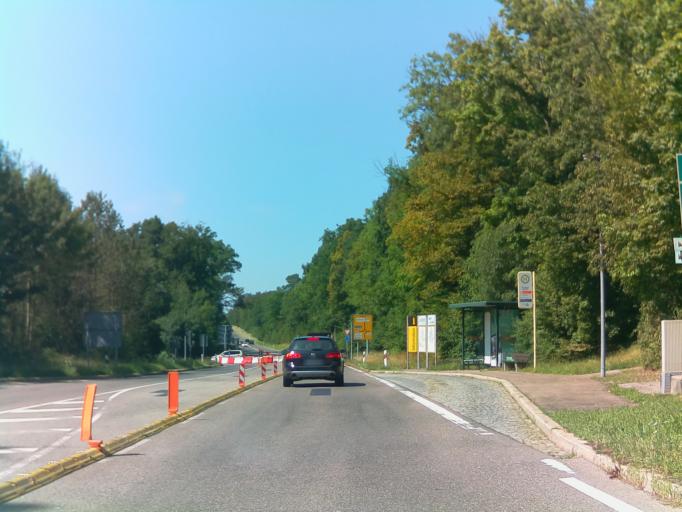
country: DE
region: Baden-Wuerttemberg
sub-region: Regierungsbezirk Stuttgart
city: Gerlingen
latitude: 48.7902
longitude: 9.0458
